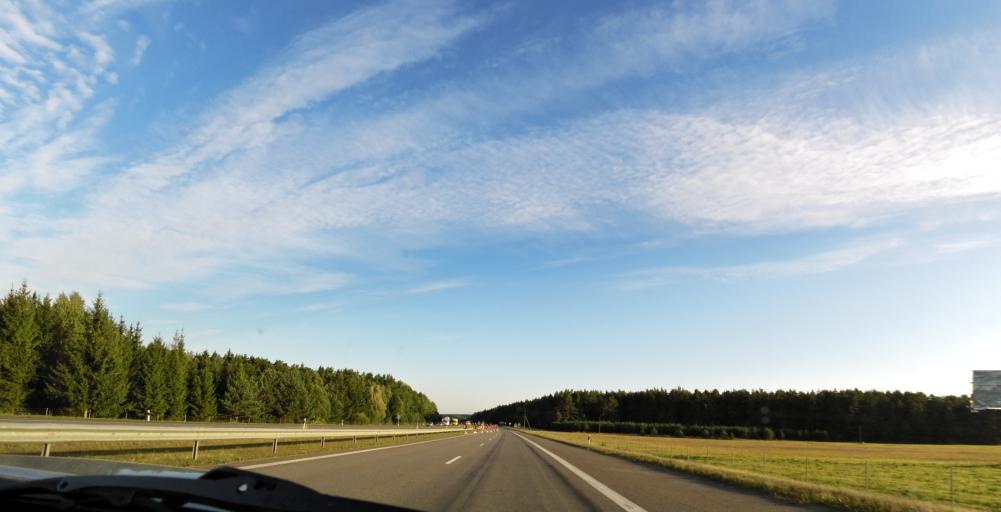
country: LT
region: Vilnius County
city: Ukmerge
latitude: 55.2394
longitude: 24.8212
